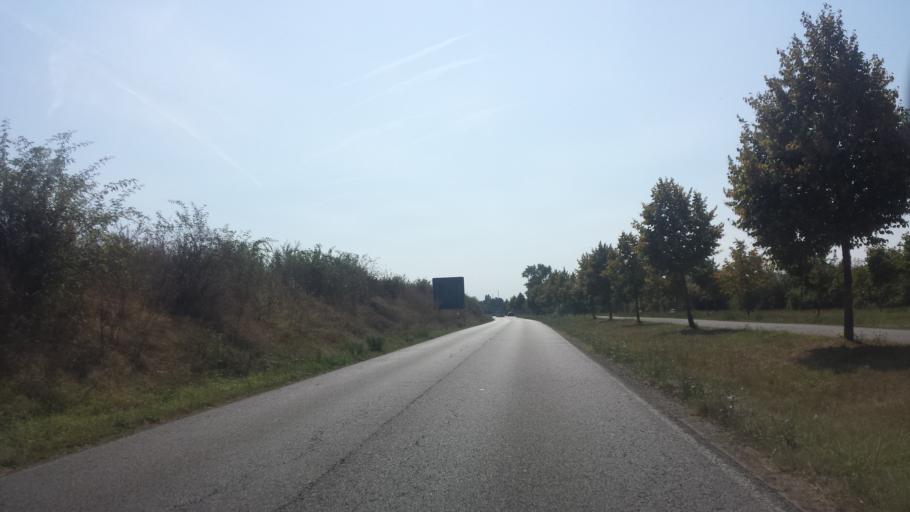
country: DE
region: Rheinland-Pfalz
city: Hassloch
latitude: 49.3616
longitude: 8.2378
